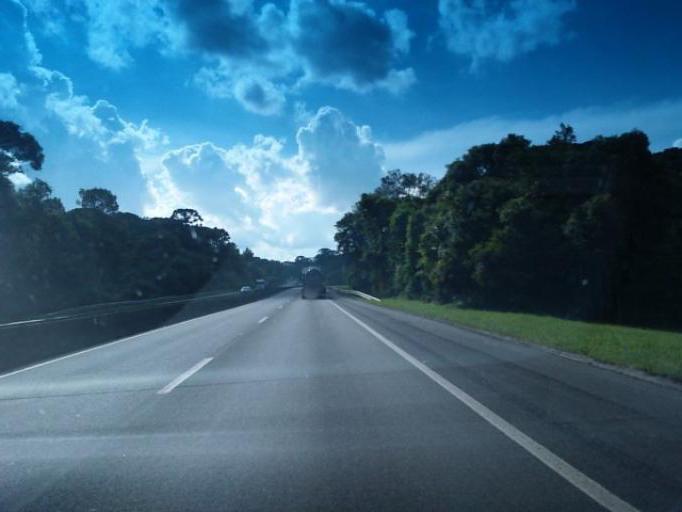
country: BR
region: Parana
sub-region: Campina Grande Do Sul
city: Campina Grande do Sul
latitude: -25.3071
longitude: -48.9875
